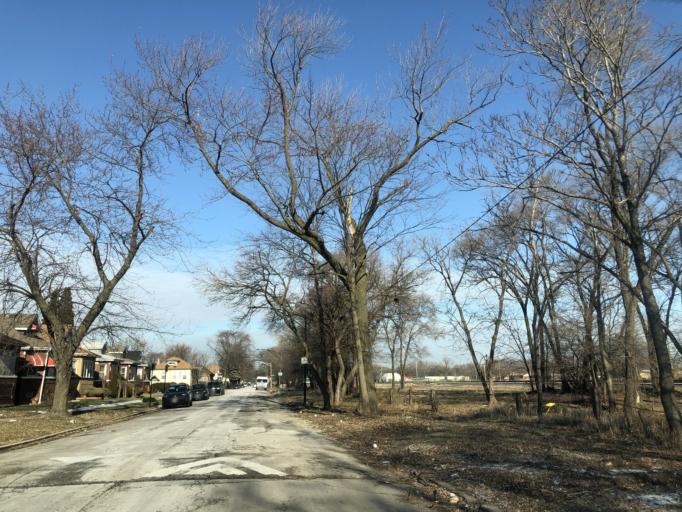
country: US
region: Illinois
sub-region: Cook County
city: Evergreen Park
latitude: 41.7615
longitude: -87.6794
